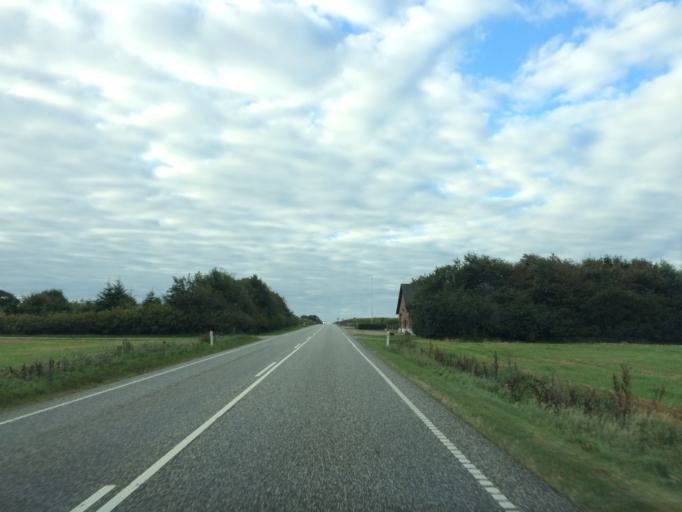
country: DK
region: Central Jutland
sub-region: Ringkobing-Skjern Kommune
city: Skjern
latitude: 56.0274
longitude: 8.5022
